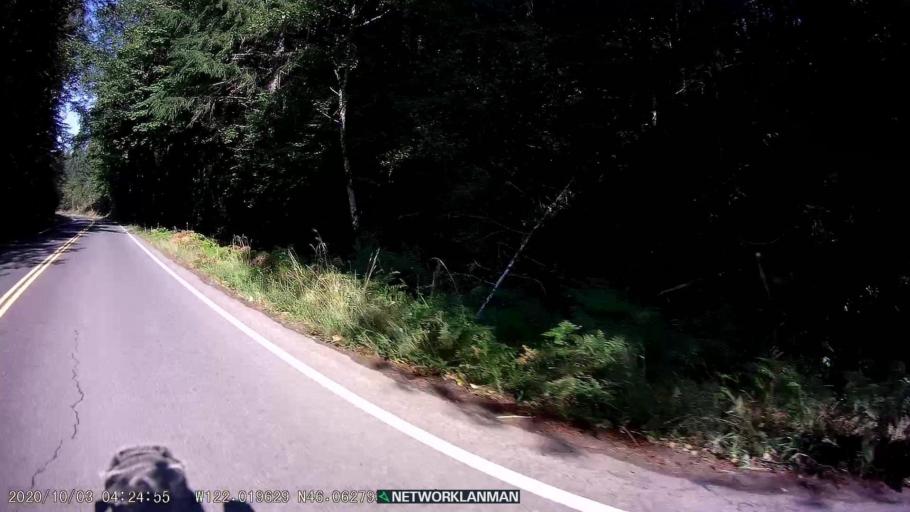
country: US
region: Washington
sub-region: Skamania County
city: Stevenson
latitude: 46.0629
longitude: -122.0195
